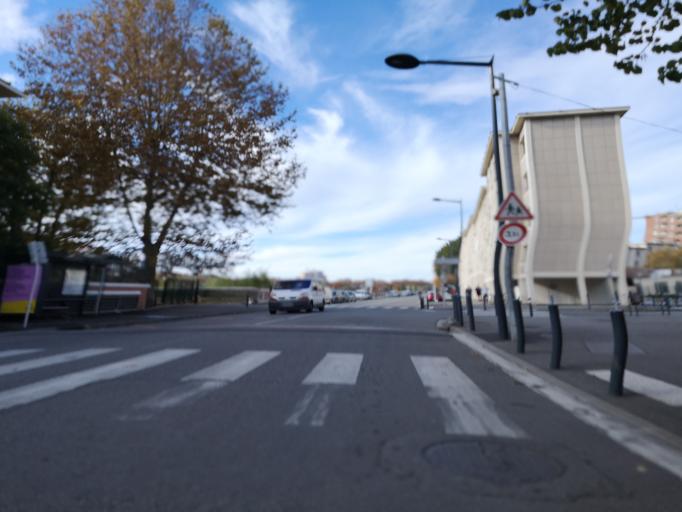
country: FR
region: Midi-Pyrenees
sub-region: Departement de la Haute-Garonne
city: Toulouse
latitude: 43.5933
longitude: 1.4429
